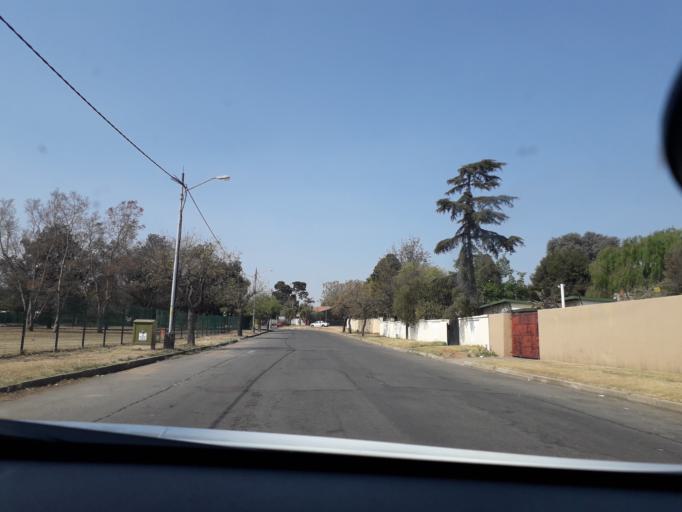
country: ZA
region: Gauteng
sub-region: City of Johannesburg Metropolitan Municipality
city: Modderfontein
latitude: -26.0931
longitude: 28.2287
